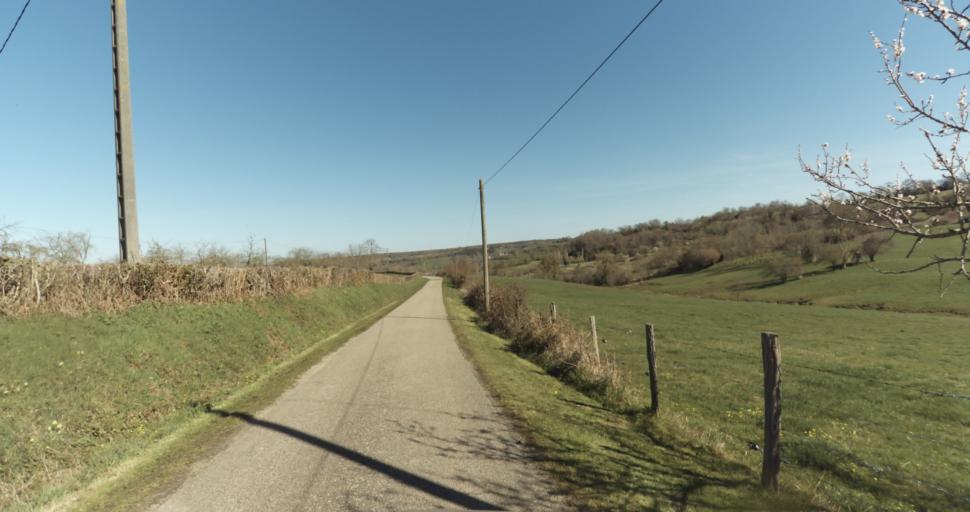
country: FR
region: Lower Normandy
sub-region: Departement du Calvados
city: Livarot
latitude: 48.9392
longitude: 0.0713
